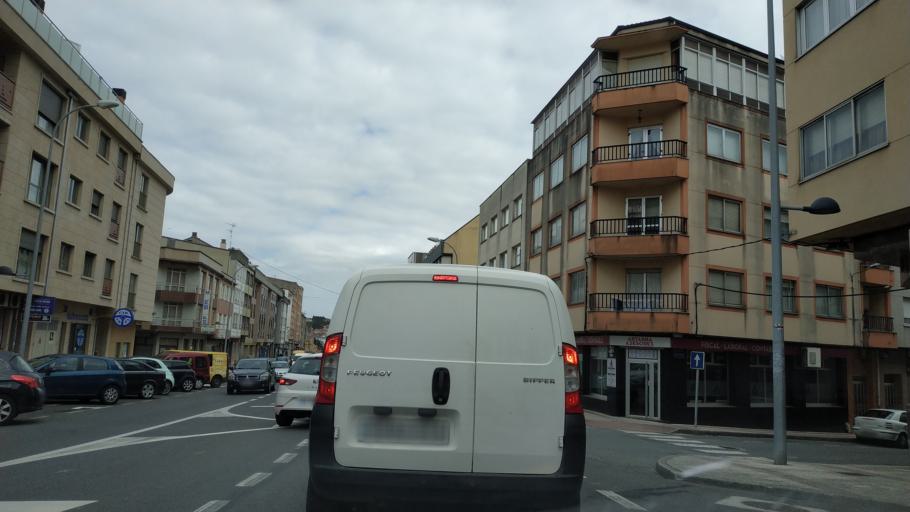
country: ES
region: Galicia
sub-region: Provincia da Coruna
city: Arteixo
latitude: 43.3037
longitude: -8.5130
